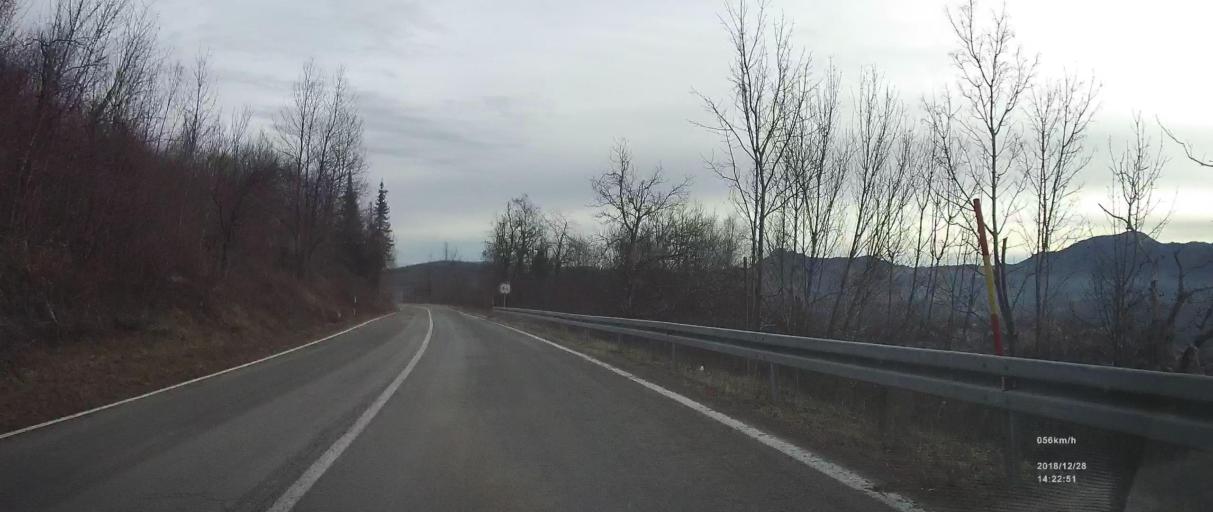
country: HR
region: Primorsko-Goranska
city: Vrbovsko
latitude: 45.3820
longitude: 15.0886
